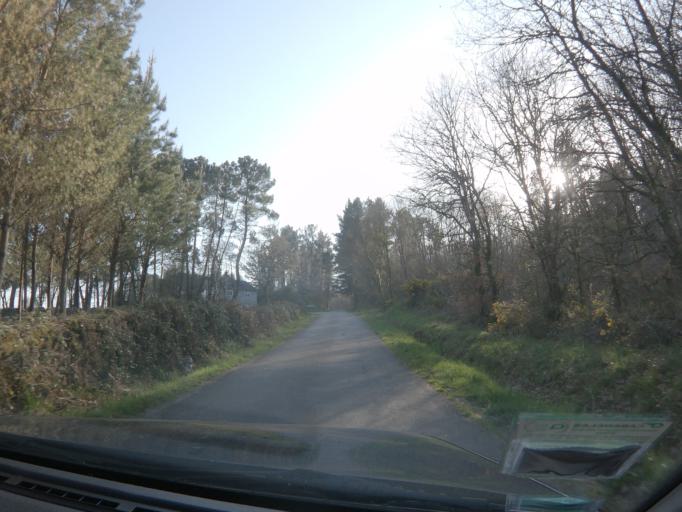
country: ES
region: Galicia
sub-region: Provincia de Lugo
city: Corgo
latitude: 42.9375
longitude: -7.4452
